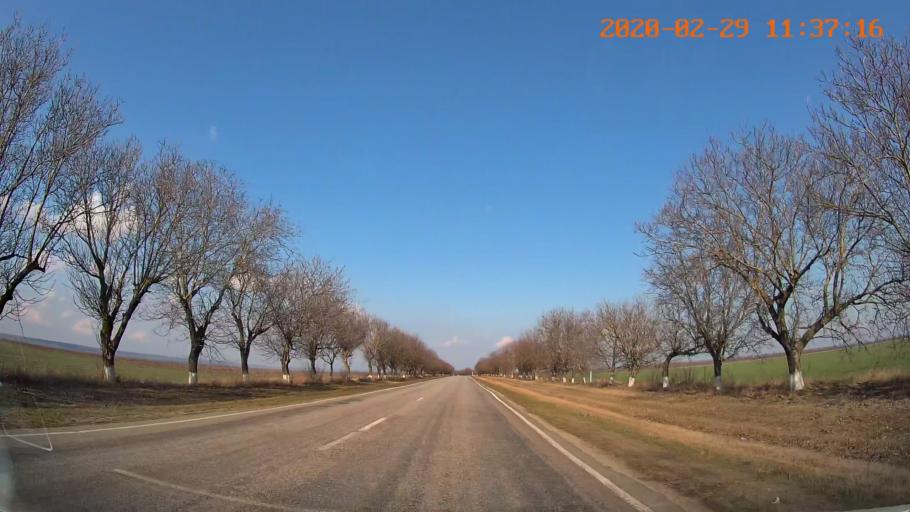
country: MD
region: Rezina
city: Saharna
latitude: 47.6092
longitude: 29.0476
